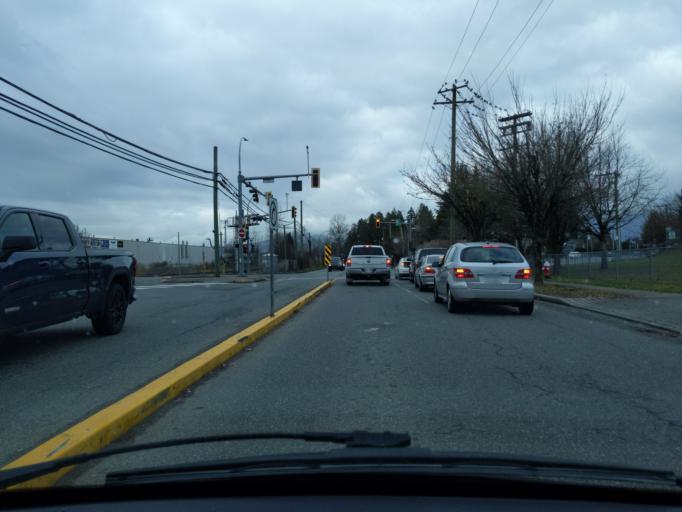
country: CA
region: British Columbia
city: Pitt Meadows
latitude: 49.2117
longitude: -122.6582
